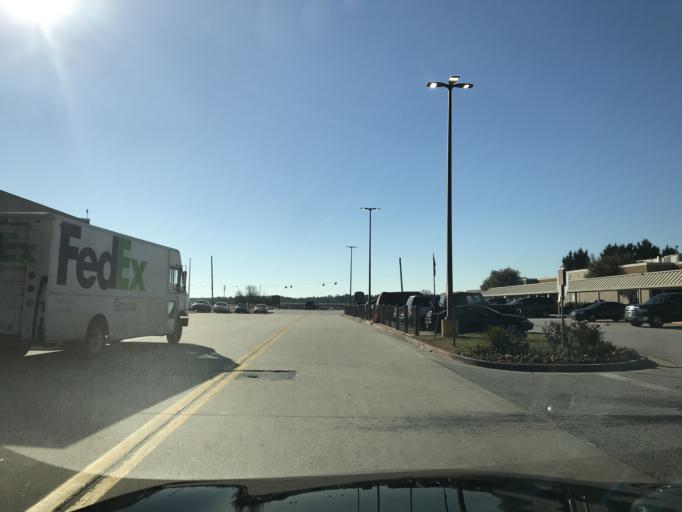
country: US
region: Georgia
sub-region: Fulton County
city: College Park
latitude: 33.6262
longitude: -84.4311
